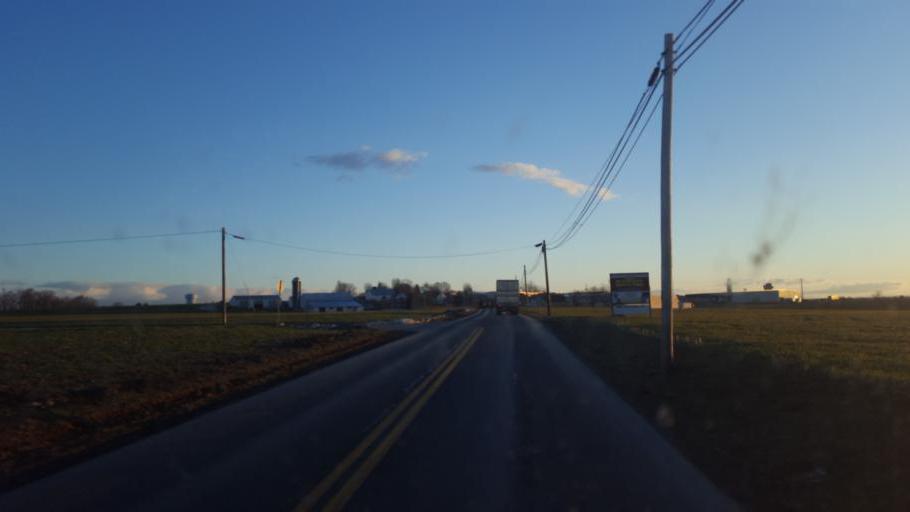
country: US
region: Pennsylvania
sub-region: Lancaster County
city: New Holland
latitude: 40.0807
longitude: -76.1013
